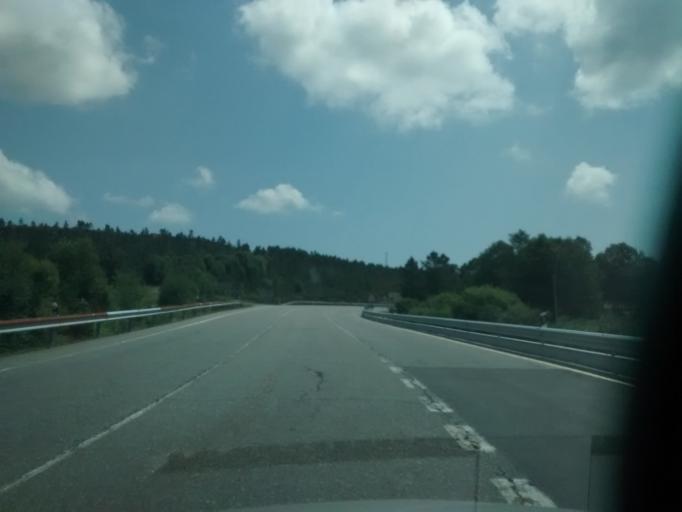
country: ES
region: Galicia
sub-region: Provincia de Pontevedra
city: Forcarei
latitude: 42.5190
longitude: -8.2844
